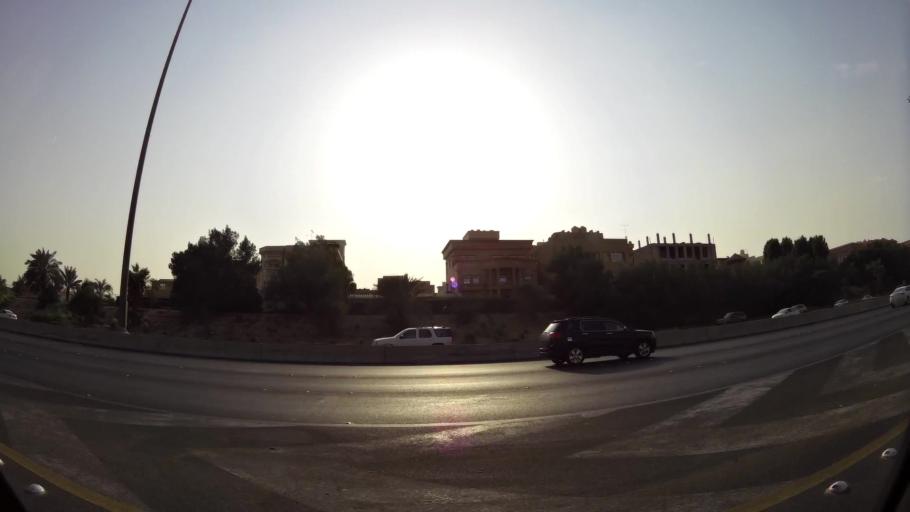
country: KW
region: Muhafazat Hawalli
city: Hawalli
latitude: 29.3202
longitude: 48.0145
